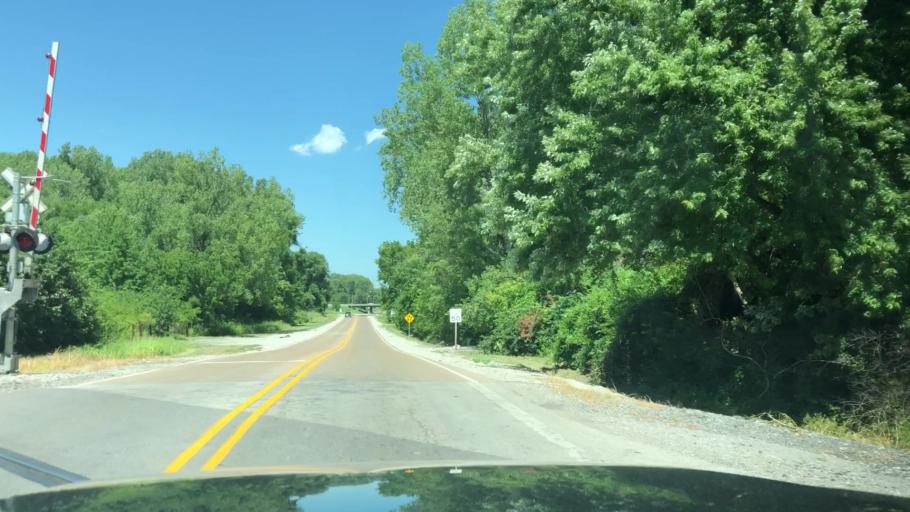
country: US
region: Illinois
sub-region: Saint Clair County
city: Centreville
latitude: 38.5633
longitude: -90.0955
